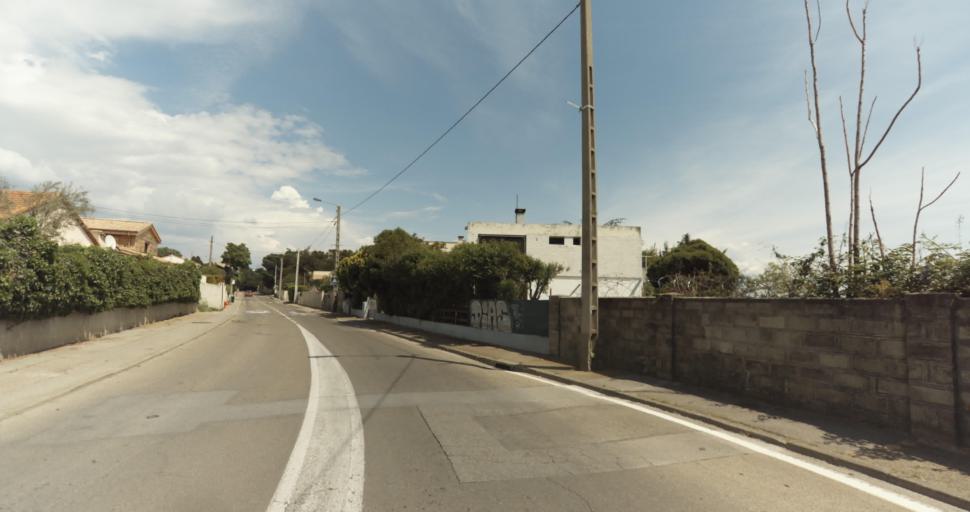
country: FR
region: Languedoc-Roussillon
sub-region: Departement du Gard
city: Rodilhan
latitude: 43.8489
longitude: 4.3932
